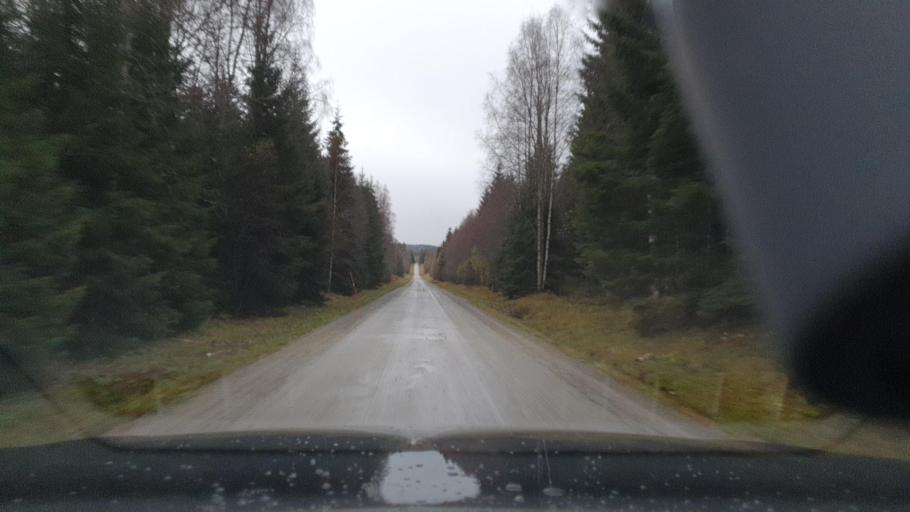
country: SE
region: Vaermland
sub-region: Arvika Kommun
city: Arvika
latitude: 59.8071
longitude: 12.7477
